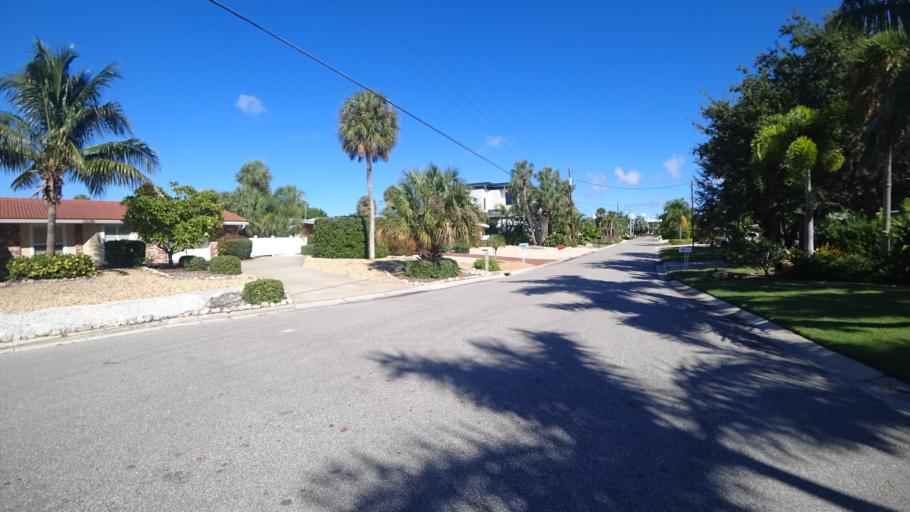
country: US
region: Florida
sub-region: Manatee County
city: Holmes Beach
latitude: 27.5181
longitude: -82.7120
